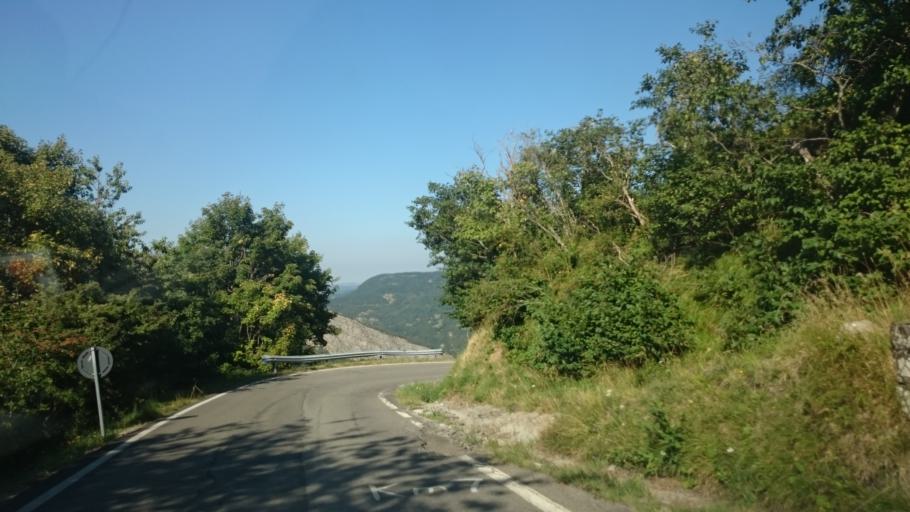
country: IT
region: Emilia-Romagna
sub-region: Provincia di Reggio Emilia
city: Villa Minozzo
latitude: 44.3001
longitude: 10.4405
